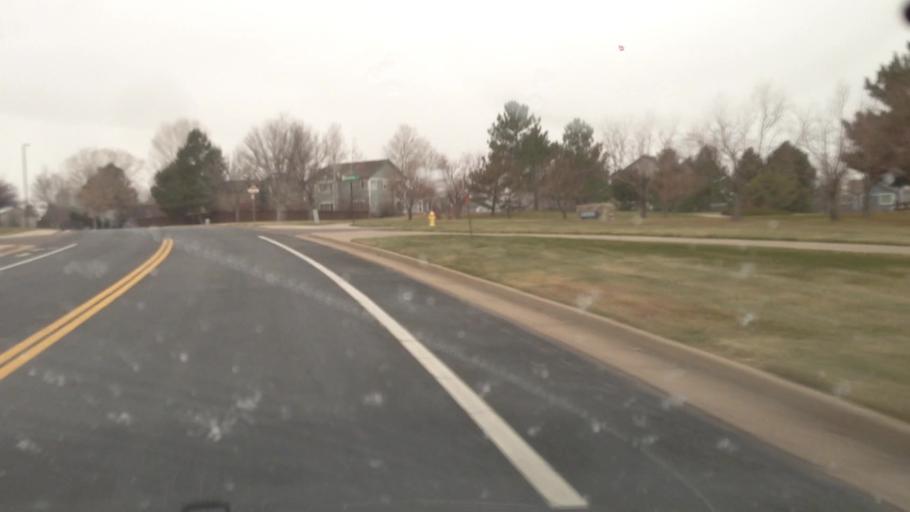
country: US
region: Colorado
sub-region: Douglas County
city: Stonegate
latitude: 39.5243
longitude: -104.7968
